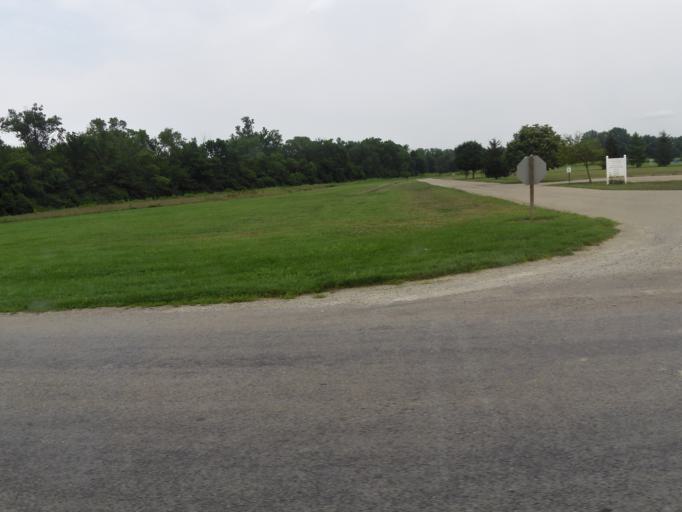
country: US
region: Ohio
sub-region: Warren County
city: Waynesville
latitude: 39.5289
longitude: -84.0826
